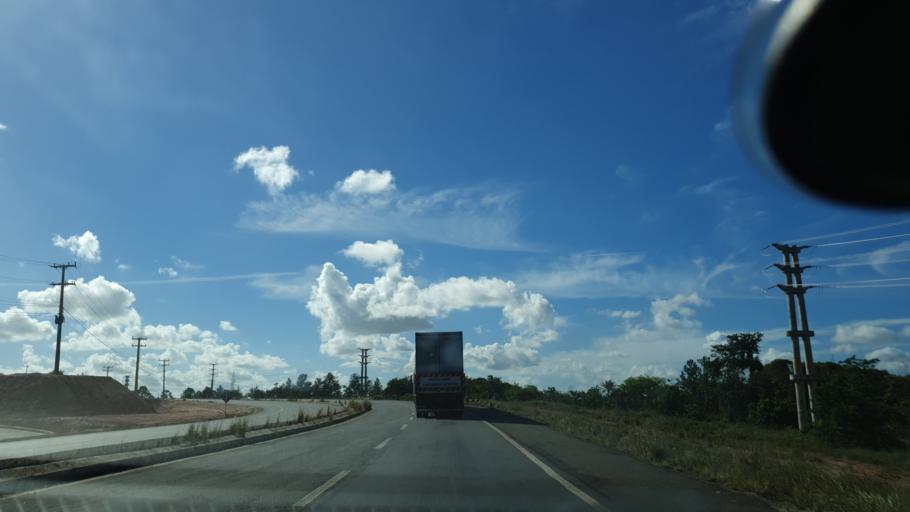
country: BR
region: Bahia
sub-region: Camacari
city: Camacari
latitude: -12.6836
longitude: -38.2645
